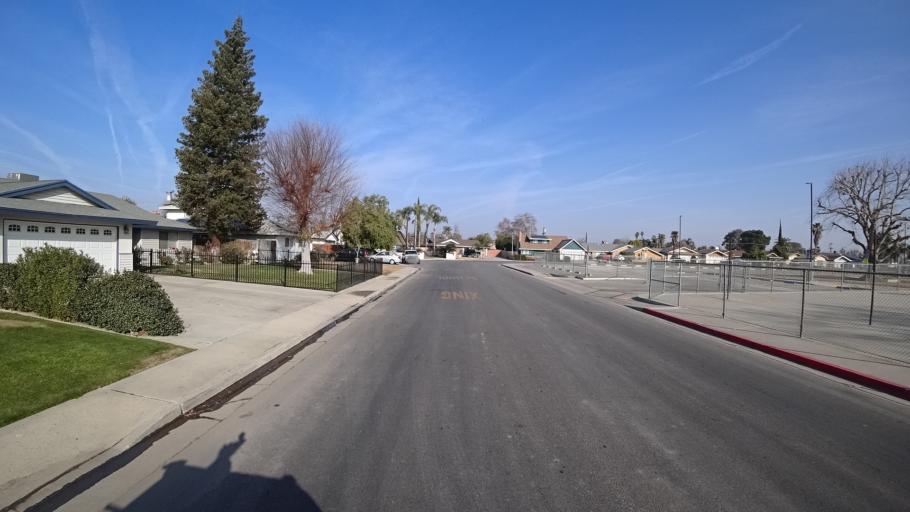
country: US
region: California
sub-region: Kern County
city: Bakersfield
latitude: 35.3260
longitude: -119.0281
